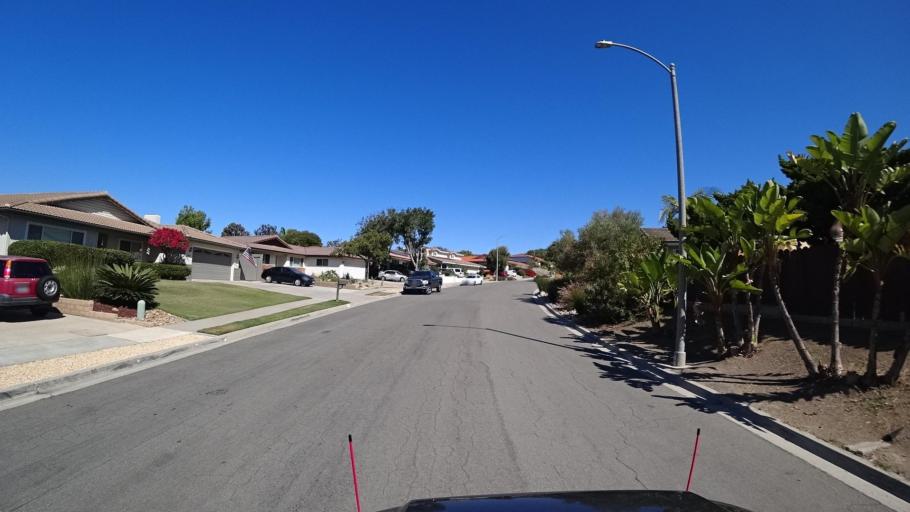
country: US
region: California
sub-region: San Diego County
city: Bonita
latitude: 32.6692
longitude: -117.0098
